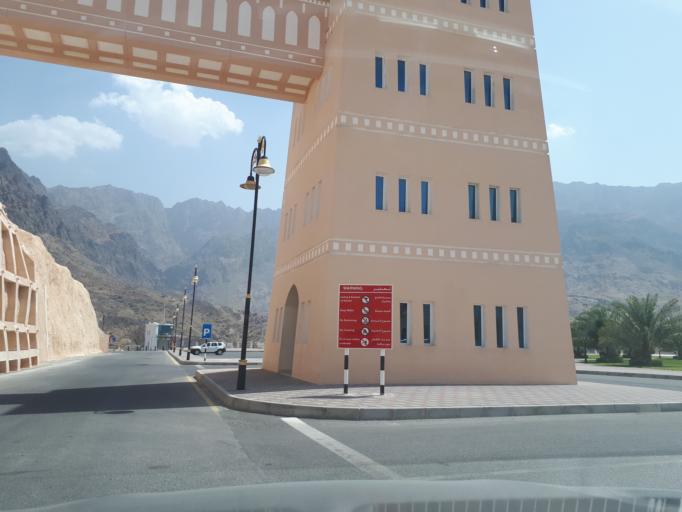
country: OM
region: Ash Sharqiyah
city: Ibra'
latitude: 23.0857
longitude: 58.8482
